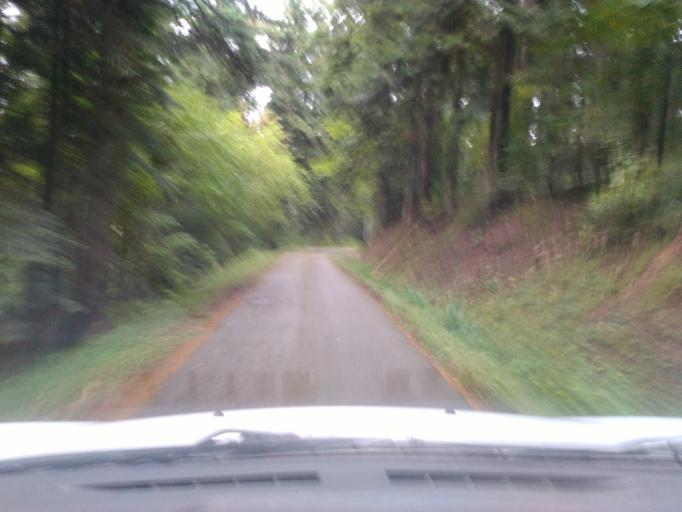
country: FR
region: Lorraine
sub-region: Departement des Vosges
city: Saint-Die-des-Vosges
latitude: 48.3033
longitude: 6.9715
